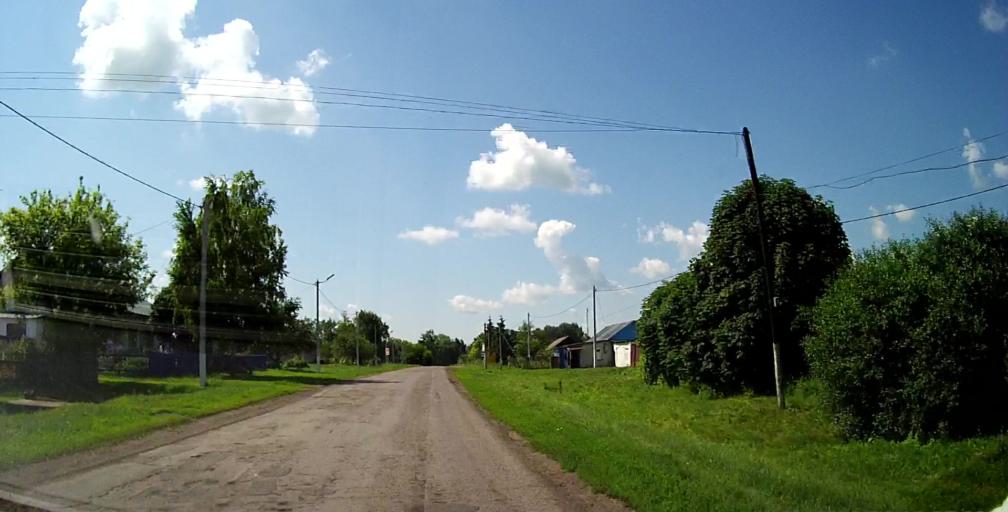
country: RU
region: Lipetsk
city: Chaplygin
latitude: 53.3741
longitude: 39.9173
